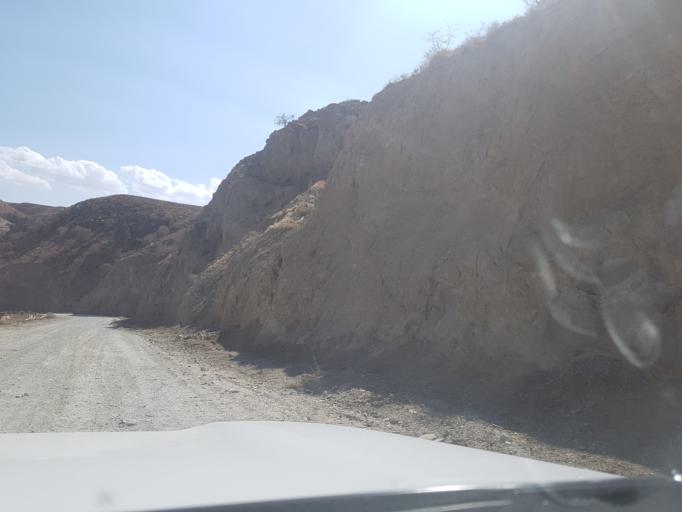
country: TM
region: Ahal
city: Baharly
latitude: 38.4442
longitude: 57.0459
